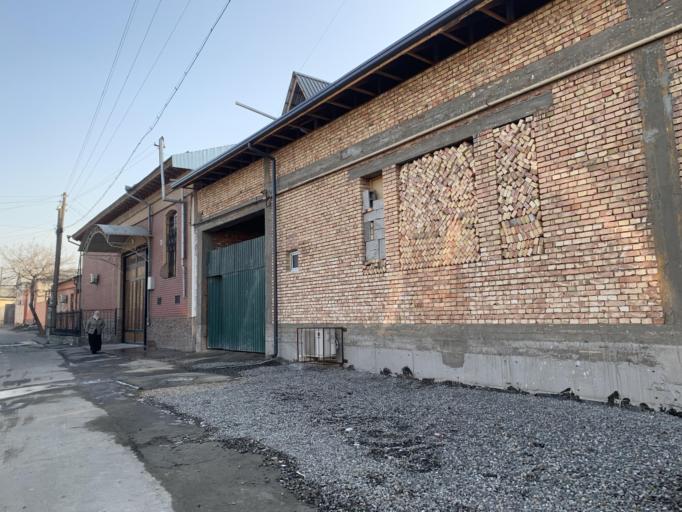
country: UZ
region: Fergana
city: Qo`qon
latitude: 40.5426
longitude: 70.9313
